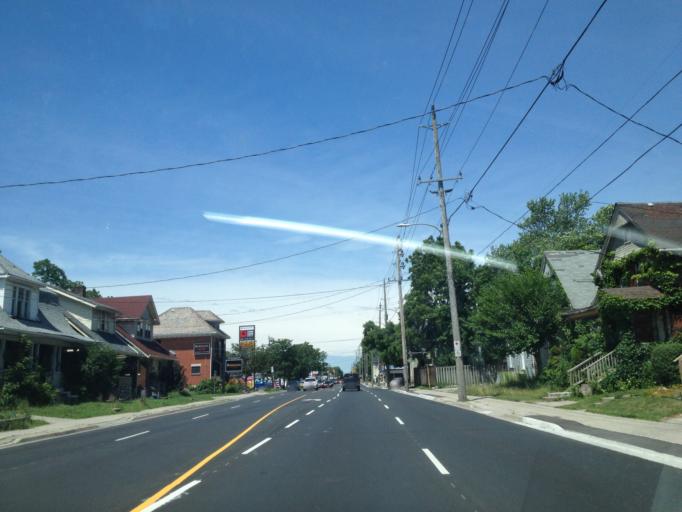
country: CA
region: Ontario
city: London
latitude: 42.9705
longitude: -81.2619
